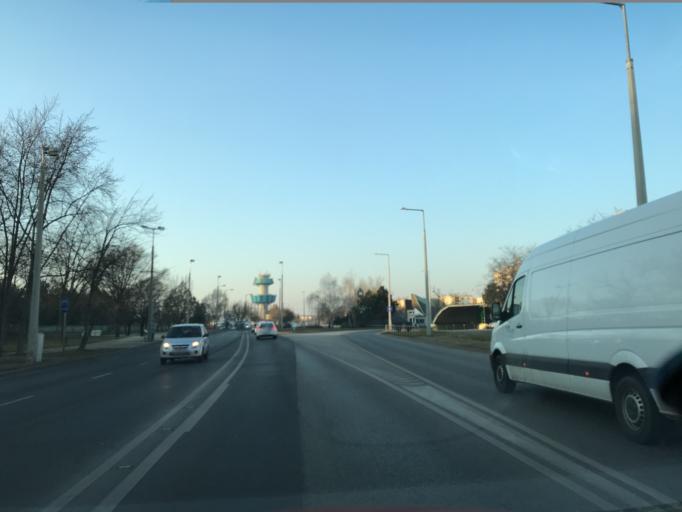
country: HU
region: Gyor-Moson-Sopron
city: Gyor
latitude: 47.6653
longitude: 17.6364
